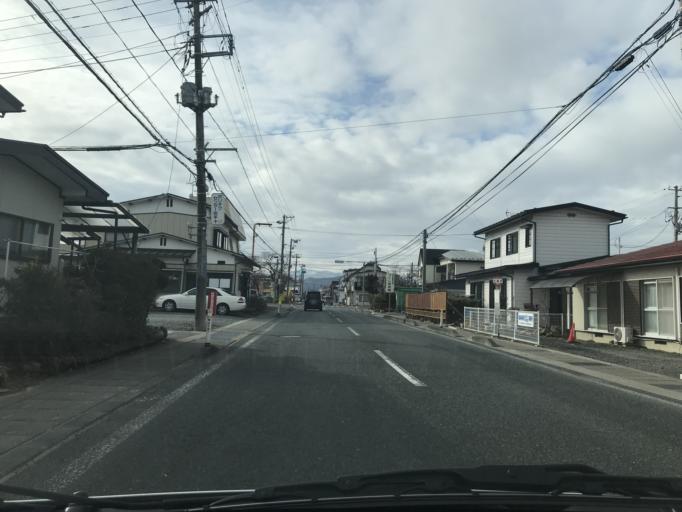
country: JP
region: Iwate
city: Hanamaki
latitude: 39.4086
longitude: 141.1042
